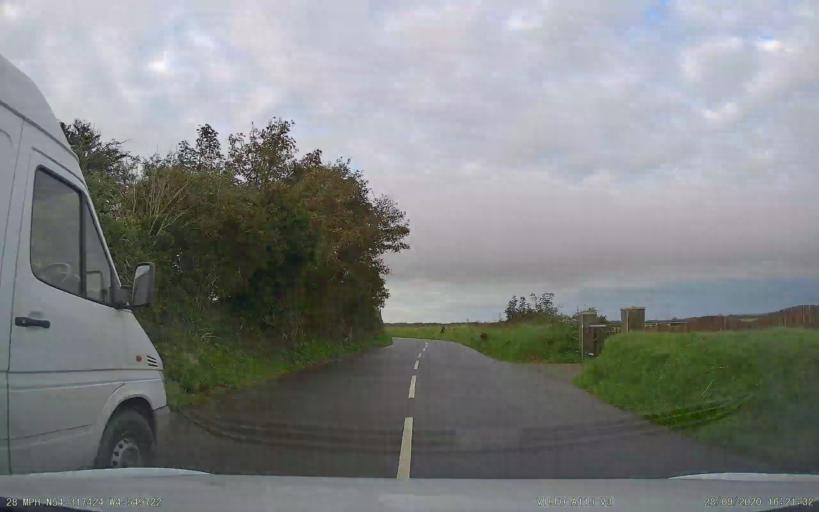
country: IM
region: Ramsey
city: Ramsey
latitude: 54.3174
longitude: -4.5497
